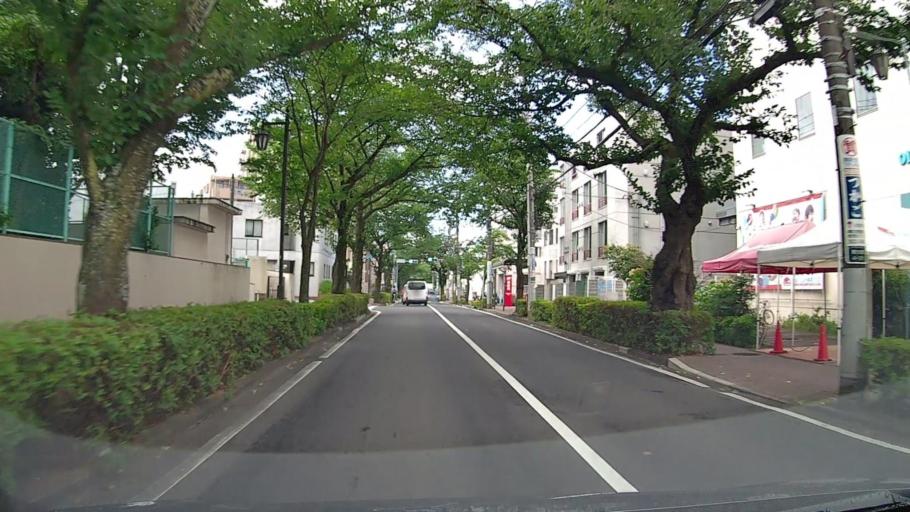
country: JP
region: Saitama
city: Wako
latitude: 35.7562
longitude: 139.5876
